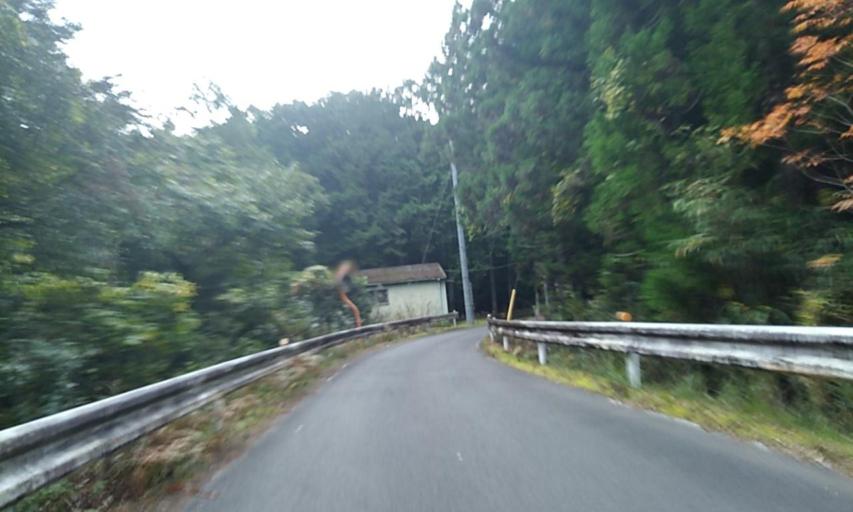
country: JP
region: Wakayama
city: Shingu
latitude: 33.9332
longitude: 135.9718
